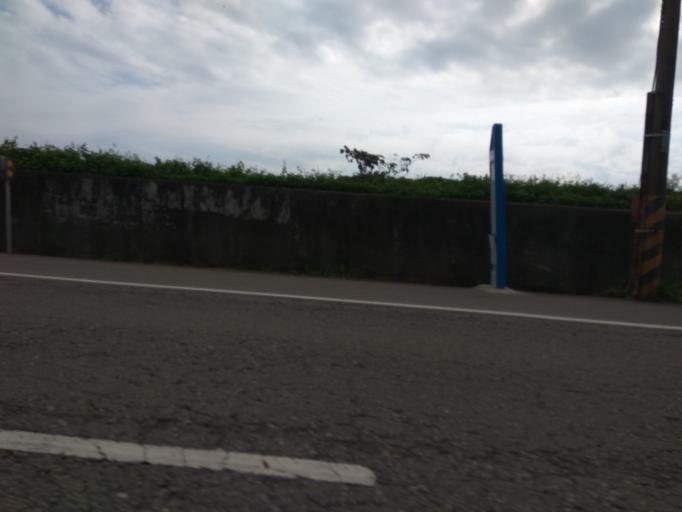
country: TW
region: Taiwan
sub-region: Hsinchu
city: Zhubei
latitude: 24.9675
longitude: 121.0180
